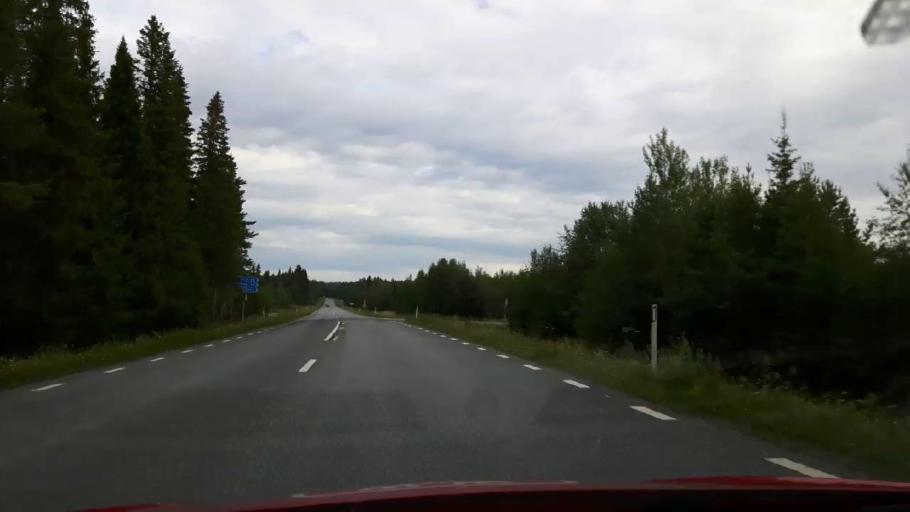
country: SE
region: Jaemtland
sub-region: Stroemsunds Kommun
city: Stroemsund
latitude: 63.5463
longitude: 15.3716
